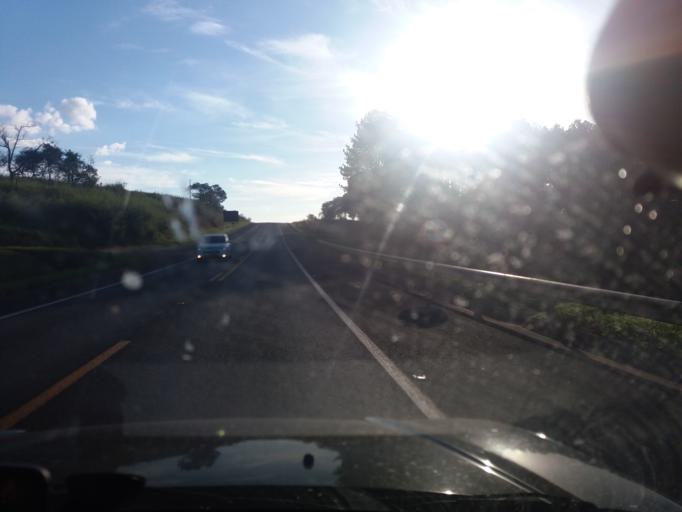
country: BR
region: Sao Paulo
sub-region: Buri
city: Buri
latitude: -23.9296
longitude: -48.6490
